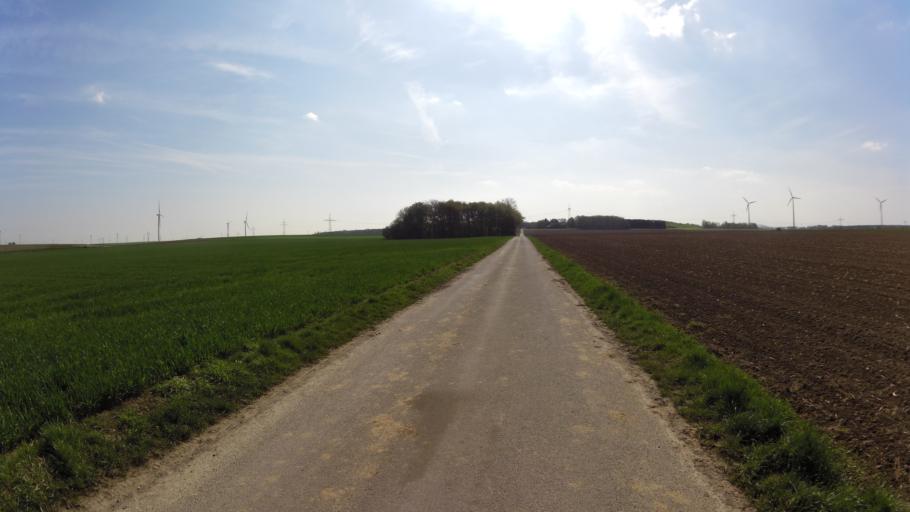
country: DE
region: North Rhine-Westphalia
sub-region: Regierungsbezirk Koln
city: Gangelt
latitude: 51.0021
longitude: 6.0614
